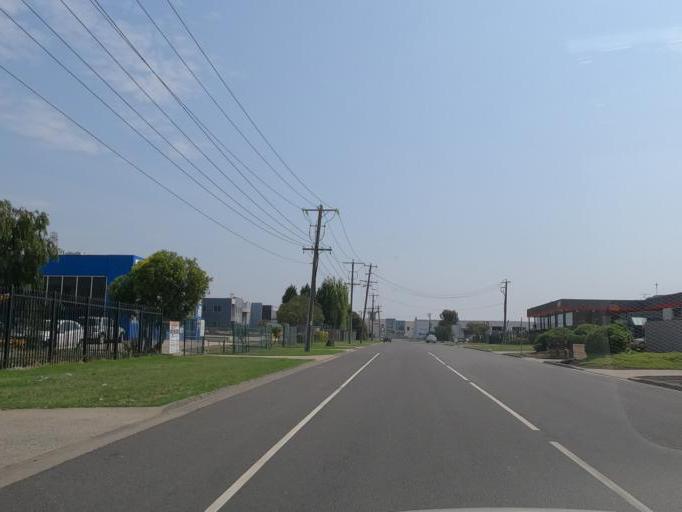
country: AU
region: Victoria
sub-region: Hume
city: Coolaroo
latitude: -37.6472
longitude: 144.9466
